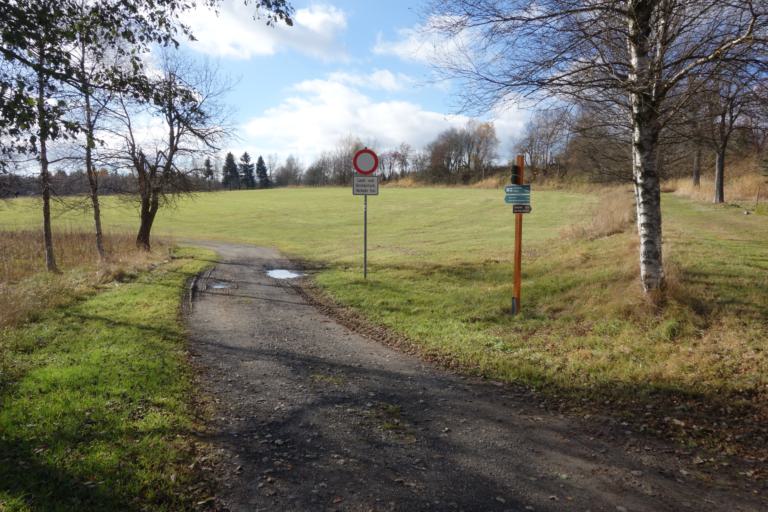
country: DE
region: Saxony
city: Pobershau
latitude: 50.5596
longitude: 13.2217
